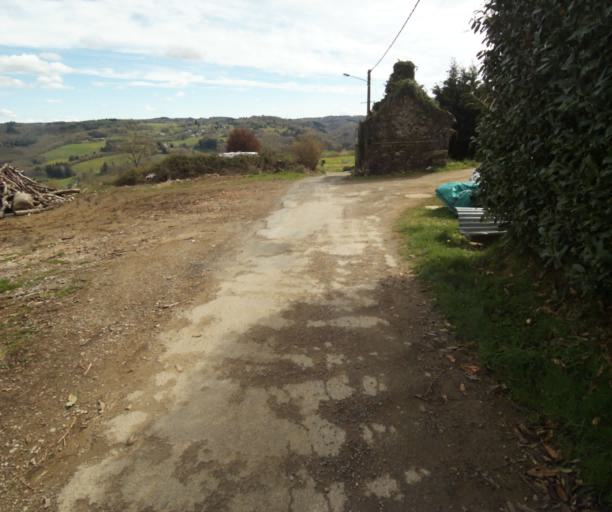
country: FR
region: Limousin
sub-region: Departement de la Correze
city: Laguenne
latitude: 45.2433
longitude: 1.8360
